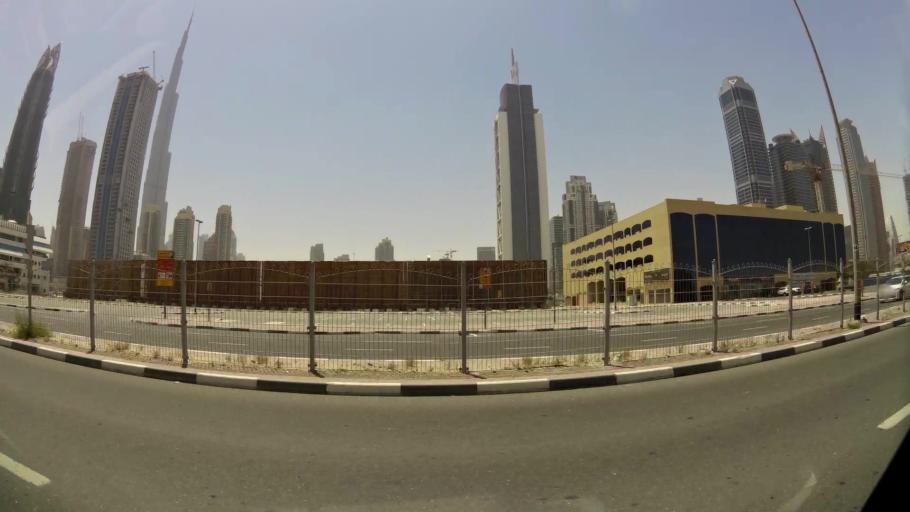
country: AE
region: Dubai
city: Dubai
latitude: 25.1981
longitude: 55.2632
